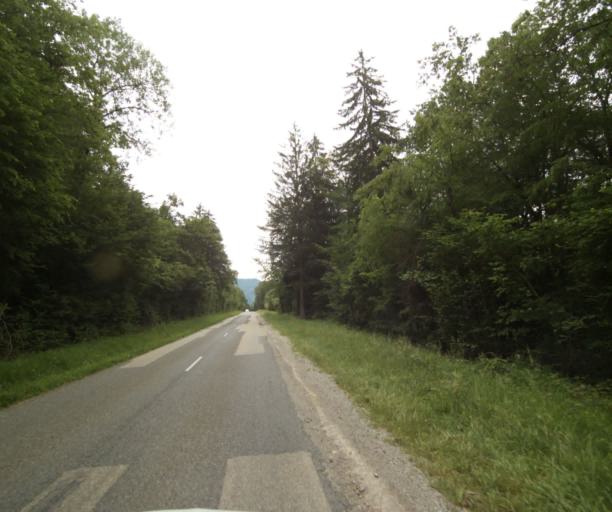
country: FR
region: Rhone-Alpes
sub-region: Departement de la Haute-Savoie
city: Sciez
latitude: 46.3104
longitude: 6.4057
